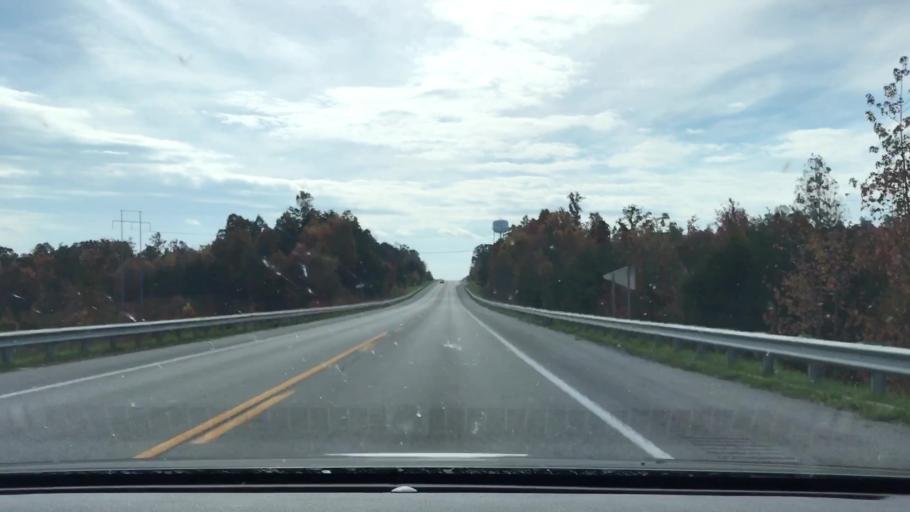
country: US
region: Kentucky
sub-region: McCreary County
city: Pine Knot
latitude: 36.6374
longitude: -84.4345
